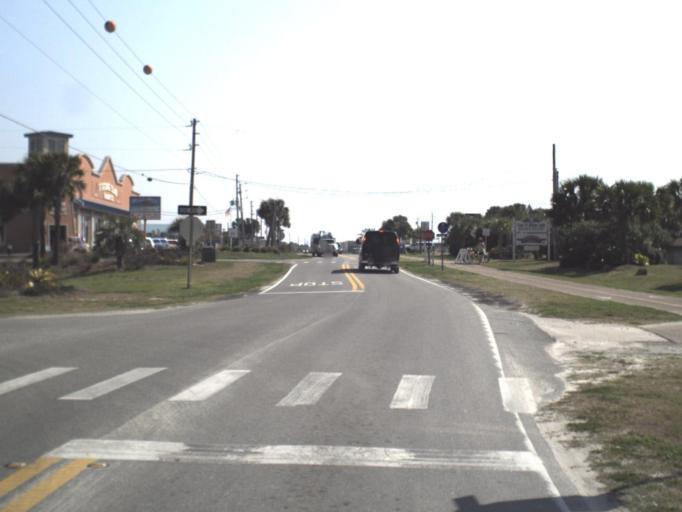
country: US
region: Florida
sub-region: Franklin County
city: Eastpoint
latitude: 29.6632
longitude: -84.8635
